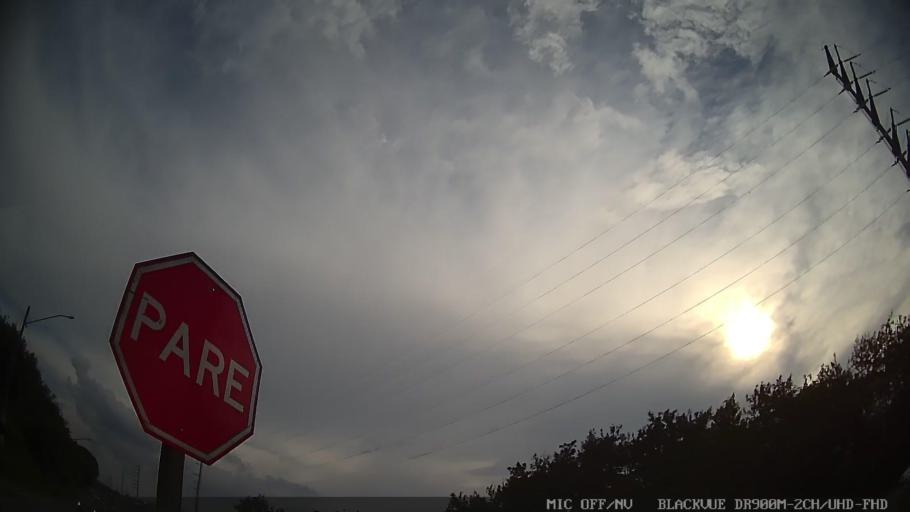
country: BR
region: Sao Paulo
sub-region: Braganca Paulista
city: Braganca Paulista
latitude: -22.9350
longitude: -46.5567
